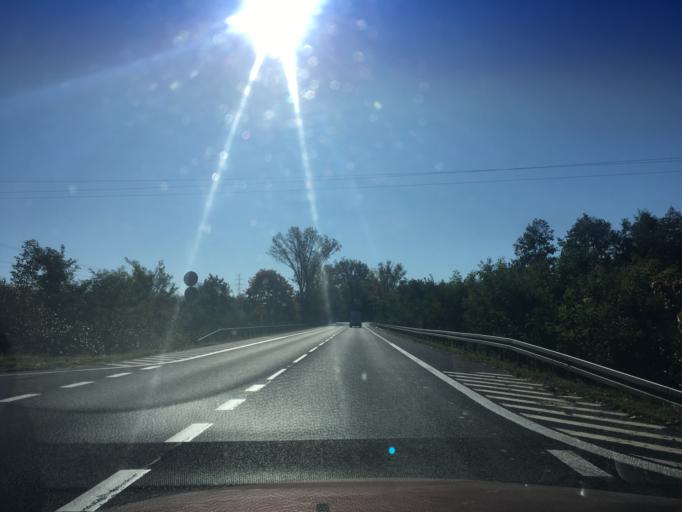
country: DE
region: Saxony
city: Ostritz
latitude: 51.0056
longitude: 14.9482
